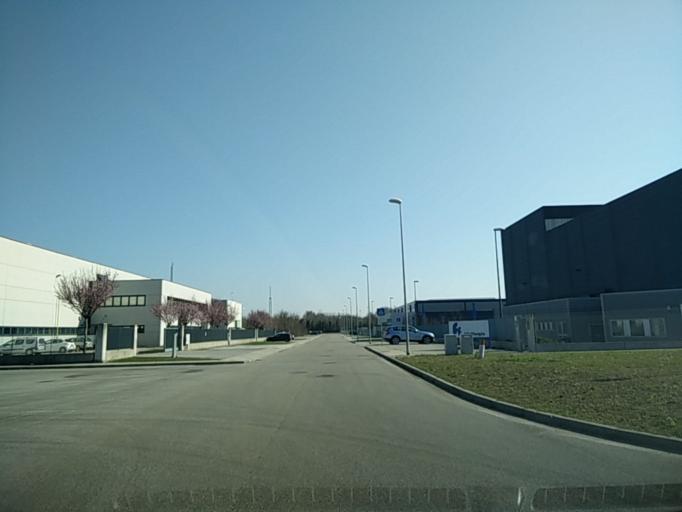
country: IT
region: Friuli Venezia Giulia
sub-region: Provincia di Udine
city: Sedegliano
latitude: 45.9924
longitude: 12.9416
